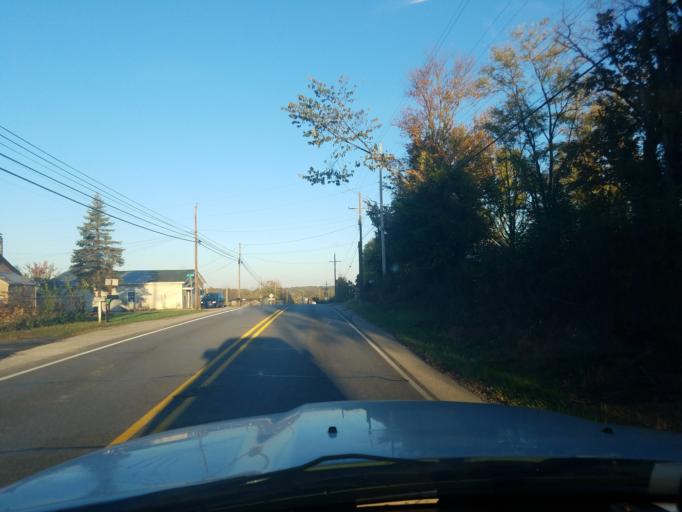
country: US
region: Indiana
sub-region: Floyd County
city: Galena
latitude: 38.3712
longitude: -85.9833
